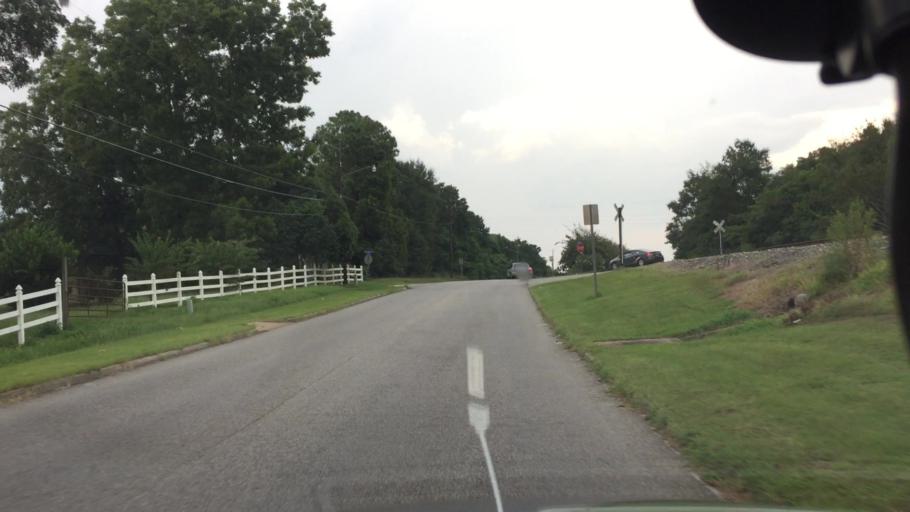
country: US
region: Alabama
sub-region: Coffee County
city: Enterprise
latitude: 31.3146
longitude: -85.8368
